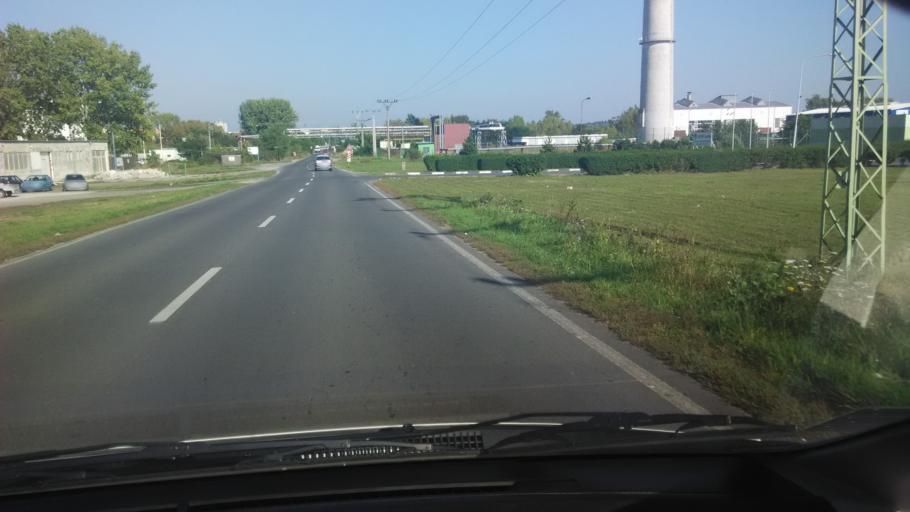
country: SK
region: Nitriansky
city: Levice
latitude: 48.1970
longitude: 18.5960
